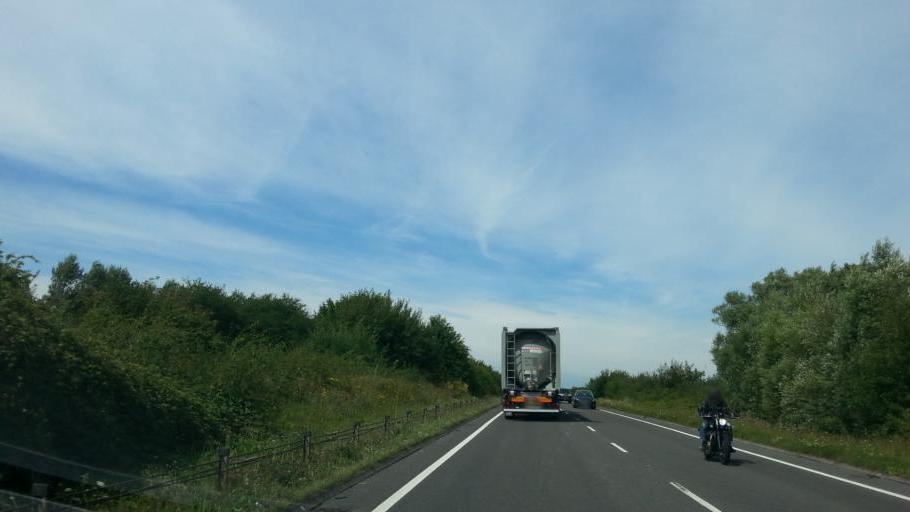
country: GB
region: England
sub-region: Suffolk
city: Exning
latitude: 52.2987
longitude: 0.3774
